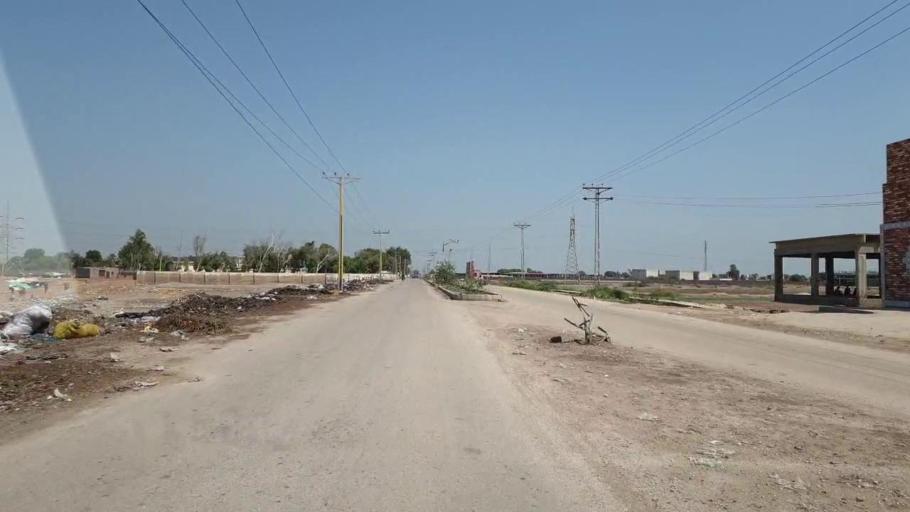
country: PK
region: Sindh
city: Hyderabad
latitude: 25.4188
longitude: 68.3863
